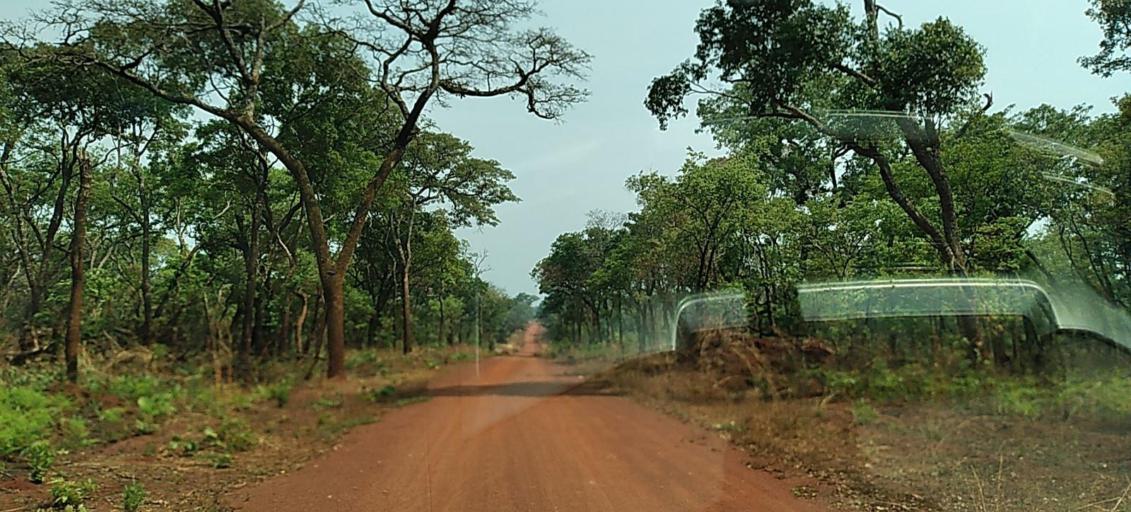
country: ZM
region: North-Western
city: Kansanshi
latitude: -11.9992
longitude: 26.8397
